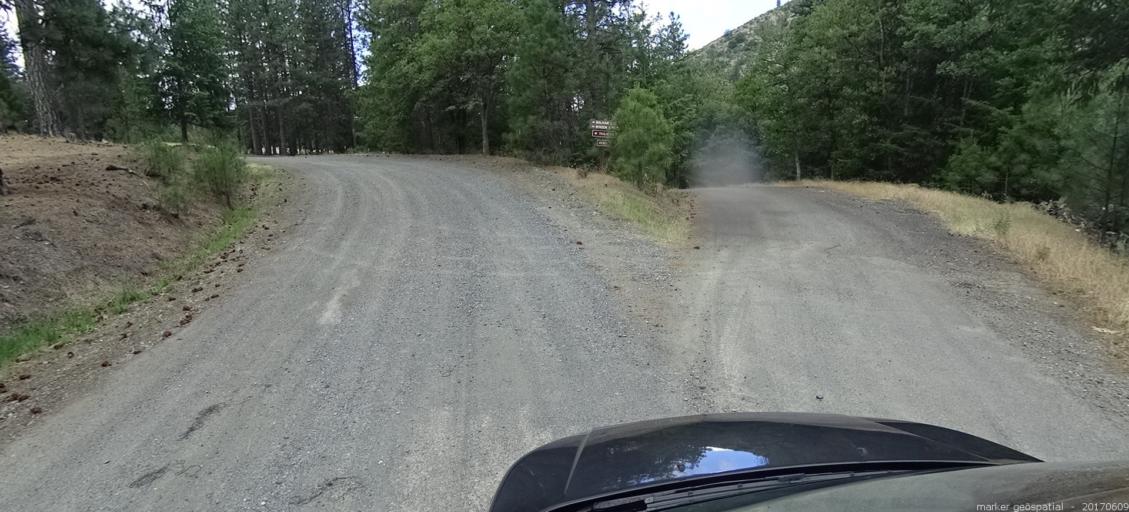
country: US
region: California
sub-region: Siskiyou County
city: Weed
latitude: 41.3009
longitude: -122.7992
